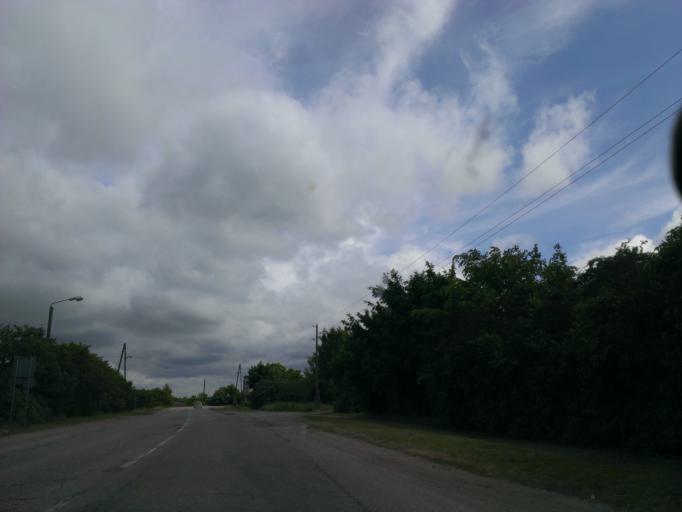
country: LV
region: Grobina
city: Grobina
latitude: 56.5330
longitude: 21.1583
